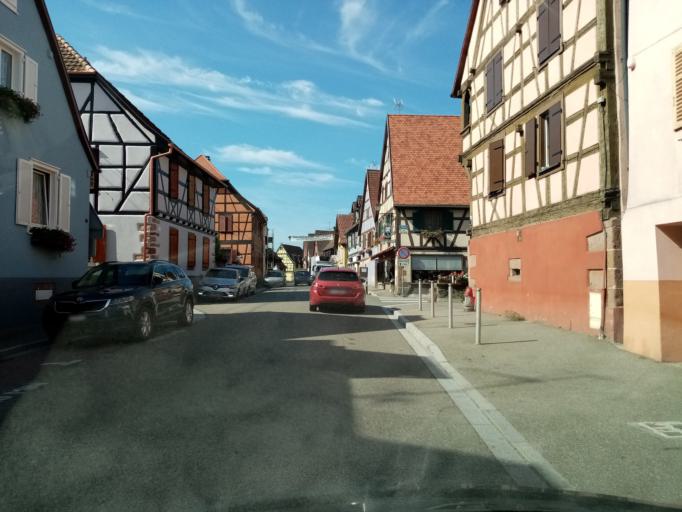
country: FR
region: Alsace
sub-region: Departement du Bas-Rhin
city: Kintzheim
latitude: 48.2543
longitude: 7.3946
